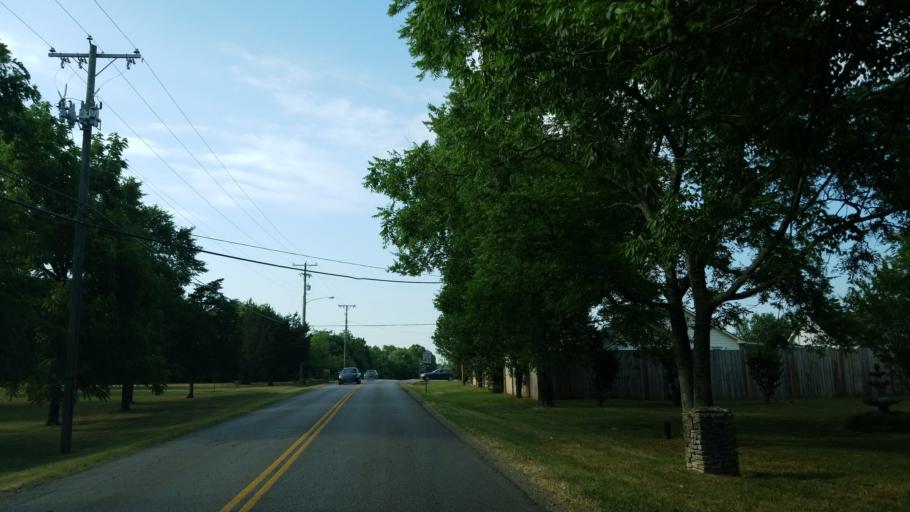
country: US
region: Tennessee
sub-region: Rutherford County
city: La Vergne
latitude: 36.0375
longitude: -86.5864
